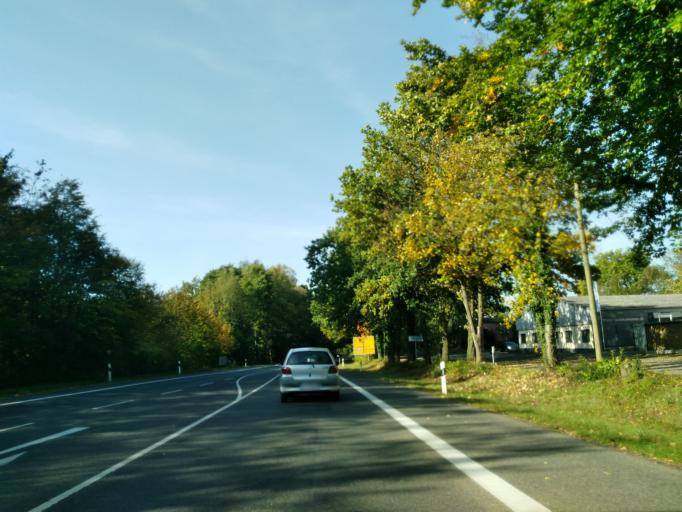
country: DE
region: North Rhine-Westphalia
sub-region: Regierungsbezirk Koln
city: Hennef
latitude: 50.7113
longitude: 7.2818
